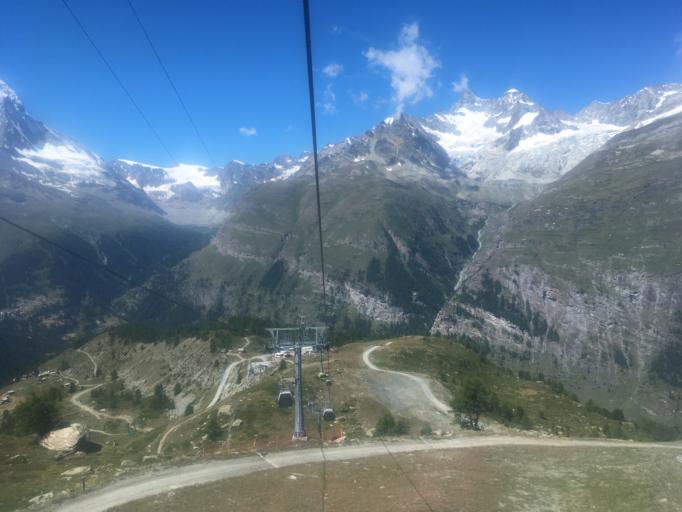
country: CH
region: Valais
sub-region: Visp District
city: Zermatt
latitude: 46.0173
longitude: 7.7772
